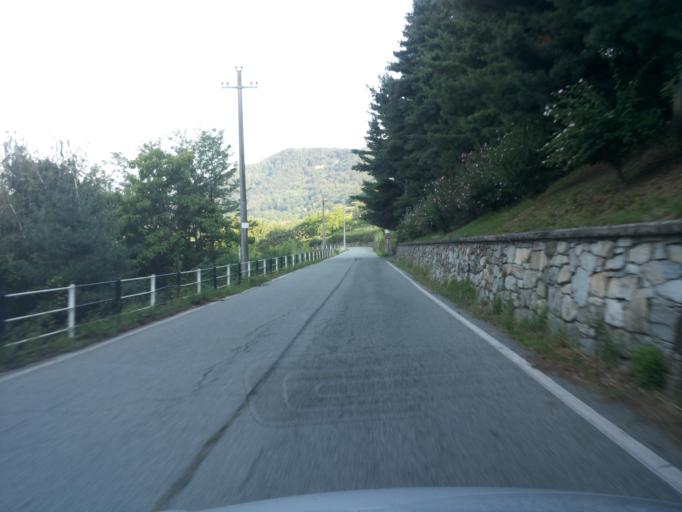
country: IT
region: Piedmont
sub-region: Provincia di Biella
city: Magnano
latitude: 45.4545
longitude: 7.9953
